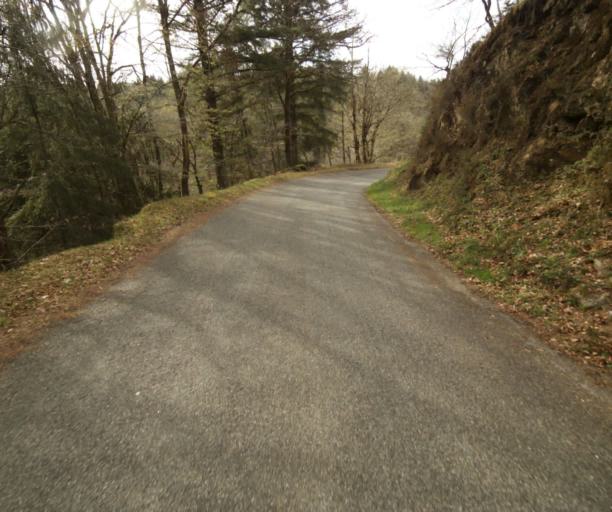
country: FR
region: Limousin
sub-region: Departement de la Correze
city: Argentat
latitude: 45.1945
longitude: 1.9791
